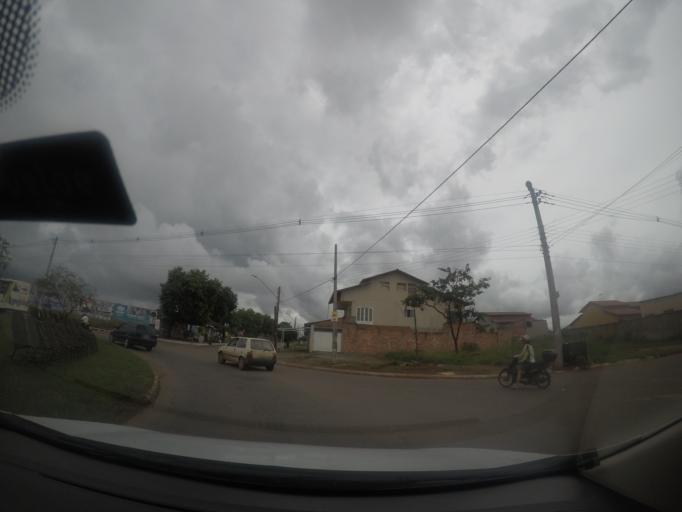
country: BR
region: Goias
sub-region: Trindade
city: Trindade
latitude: -16.6553
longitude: -49.3818
